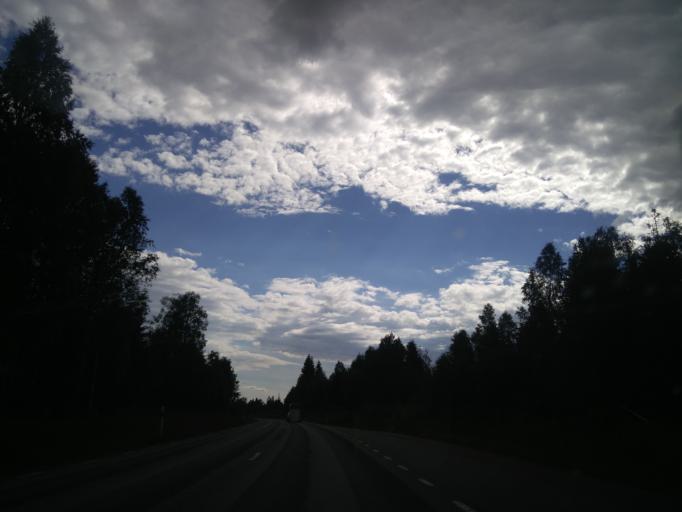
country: SE
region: Vaermland
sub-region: Filipstads Kommun
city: Filipstad
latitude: 59.7844
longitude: 14.3021
